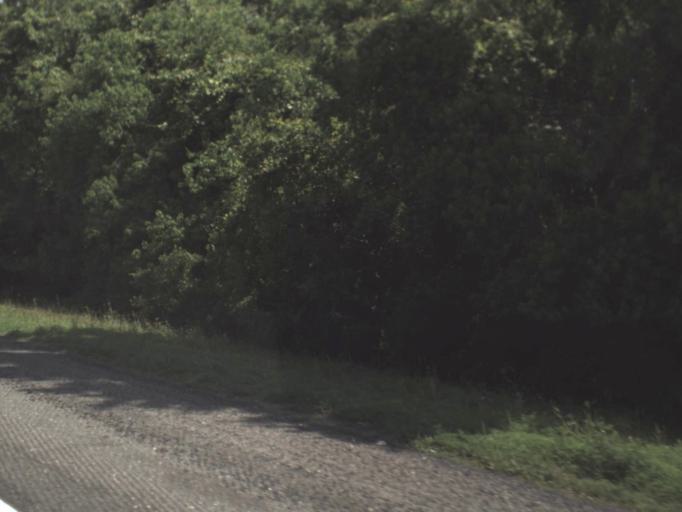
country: US
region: Florida
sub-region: Nassau County
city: Yulee
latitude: 30.5631
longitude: -81.6426
